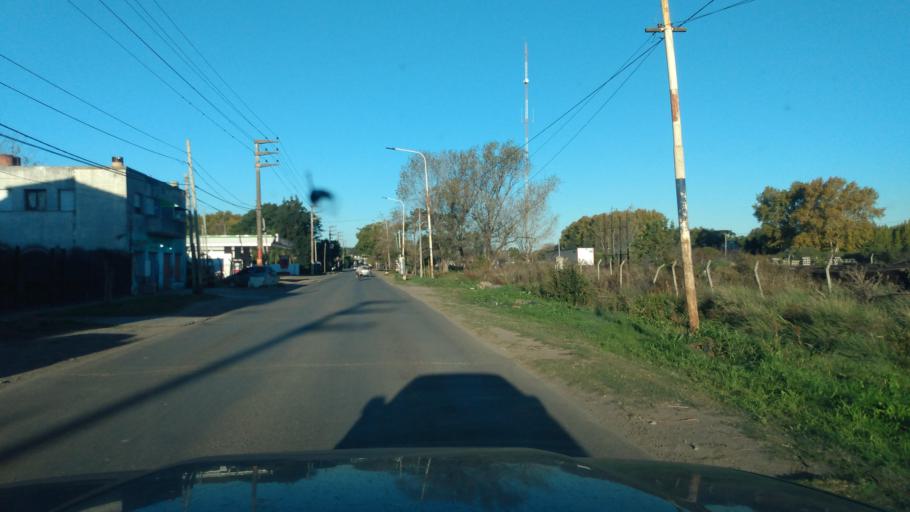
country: AR
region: Buenos Aires
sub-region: Partido de General Rodriguez
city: General Rodriguez
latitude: -34.6306
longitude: -58.8577
